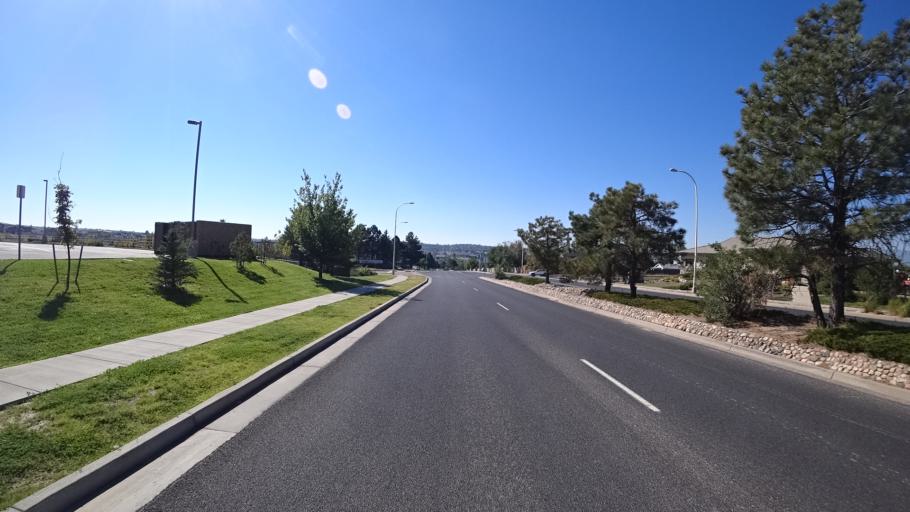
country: US
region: Colorado
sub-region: El Paso County
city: Black Forest
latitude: 38.9369
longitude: -104.7564
